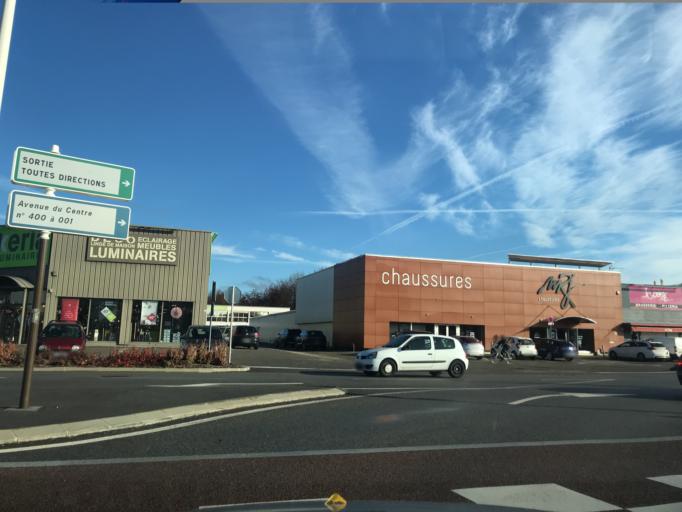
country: FR
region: Rhone-Alpes
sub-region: Departement de la Haute-Savoie
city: Epagny
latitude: 45.9365
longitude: 6.0800
